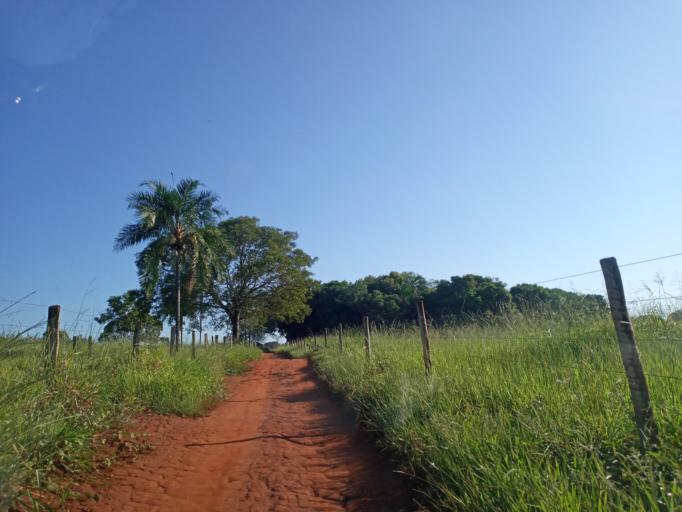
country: BR
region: Minas Gerais
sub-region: Ituiutaba
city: Ituiutaba
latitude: -18.9763
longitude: -49.4961
